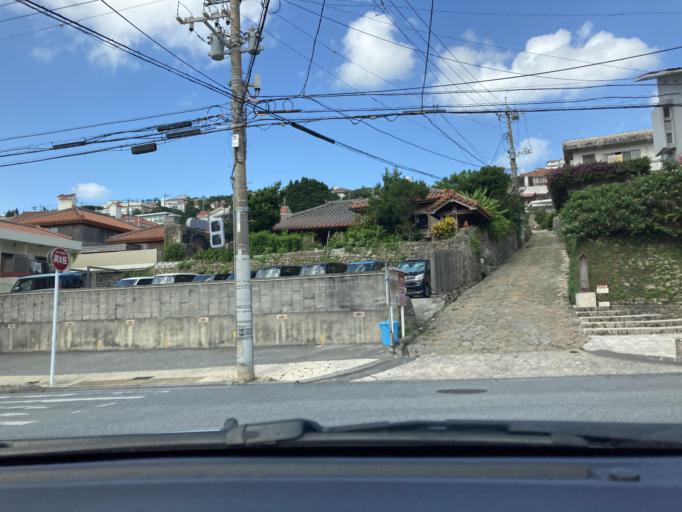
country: JP
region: Okinawa
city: Naha-shi
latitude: 26.2142
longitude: 127.7140
